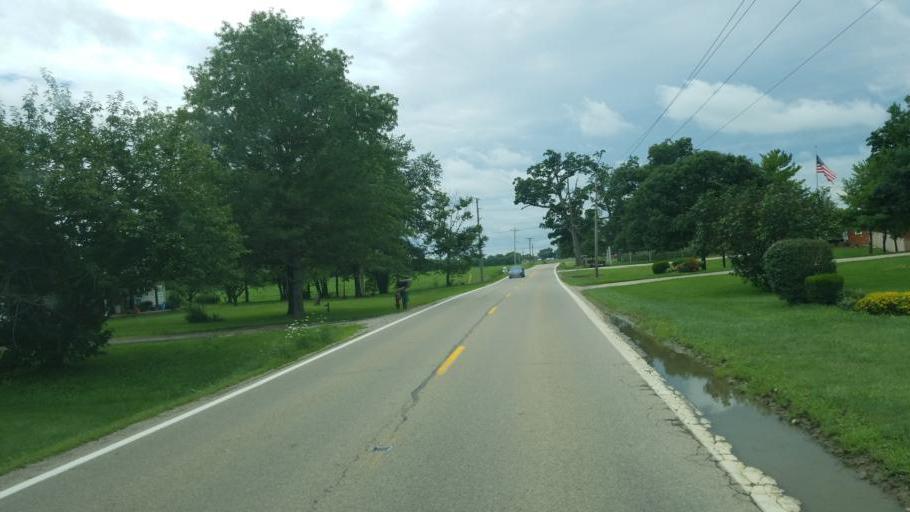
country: US
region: Ohio
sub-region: Pickaway County
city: South Bloomfield
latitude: 39.7236
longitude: -82.9709
